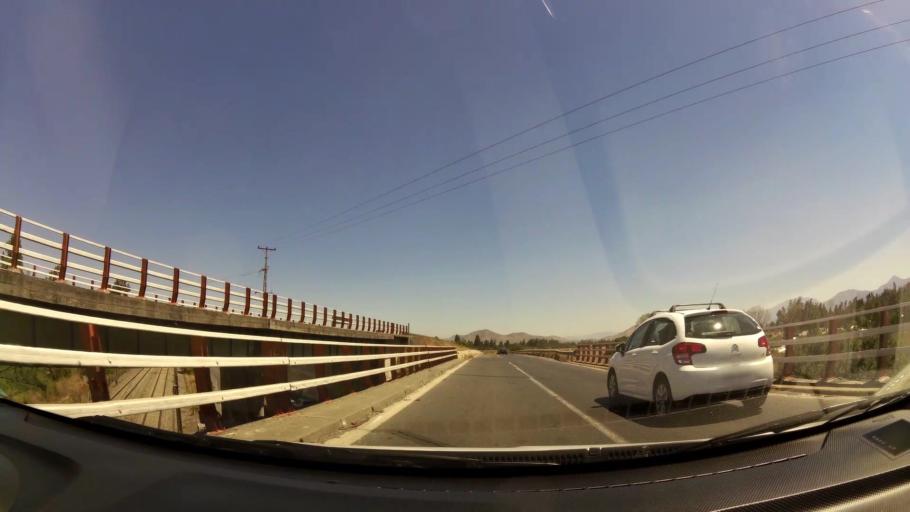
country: CL
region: O'Higgins
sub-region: Provincia de Cachapoal
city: Rancagua
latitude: -34.2313
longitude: -70.7869
